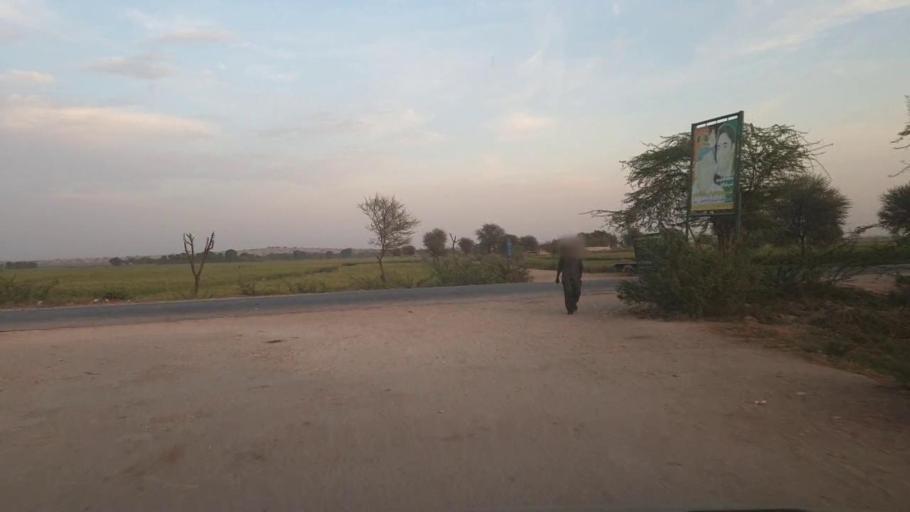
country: PK
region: Sindh
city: Umarkot
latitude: 25.2791
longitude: 69.6968
